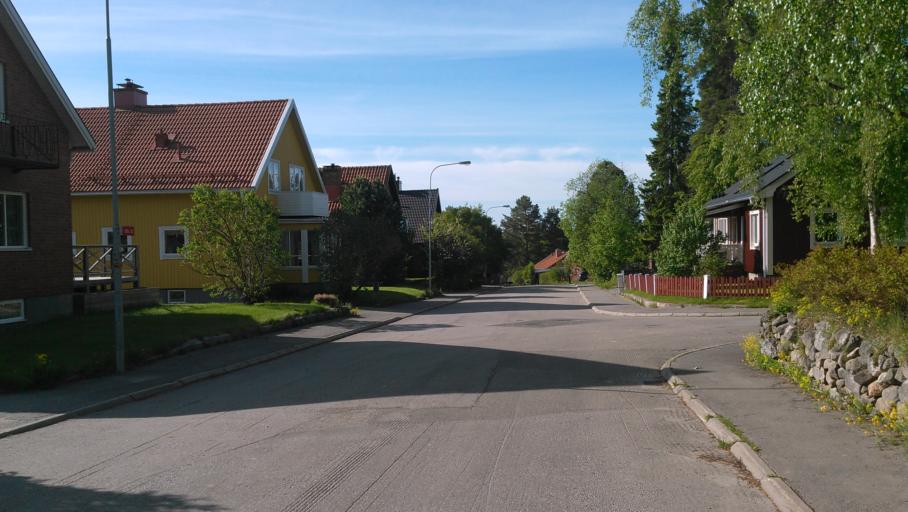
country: SE
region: Vaesterbotten
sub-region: Umea Kommun
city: Umea
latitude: 63.8108
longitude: 20.2978
